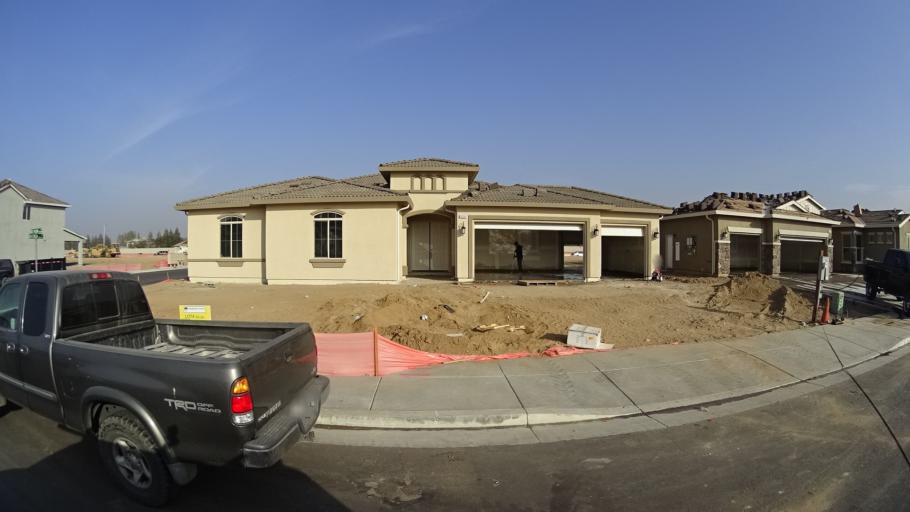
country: US
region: California
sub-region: Kern County
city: Greenacres
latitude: 35.4328
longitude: -119.1026
